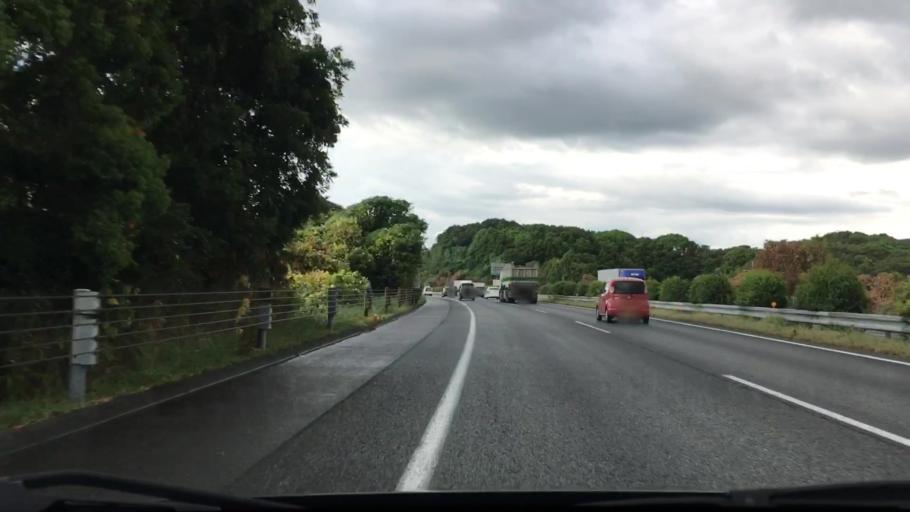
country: JP
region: Fukuoka
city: Koga
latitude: 33.7241
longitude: 130.5014
